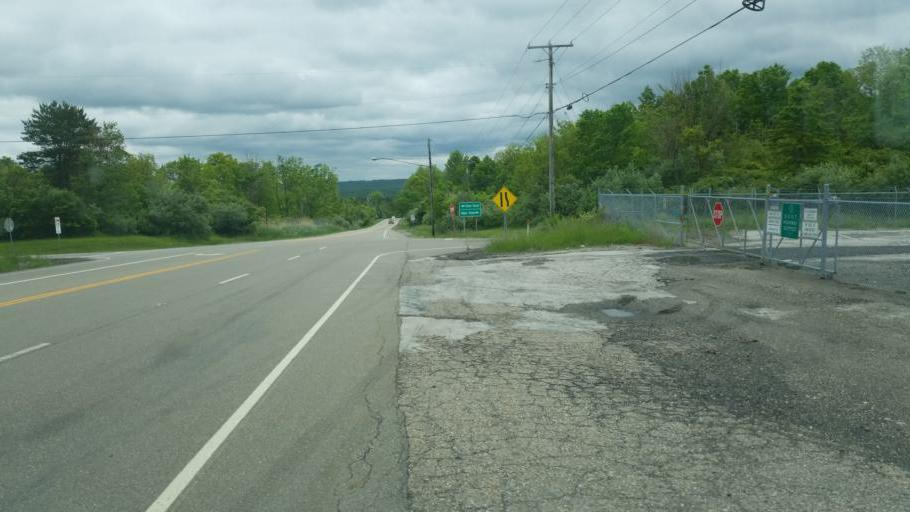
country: US
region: Ohio
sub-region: Summit County
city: Peninsula
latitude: 41.2453
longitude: -81.5877
